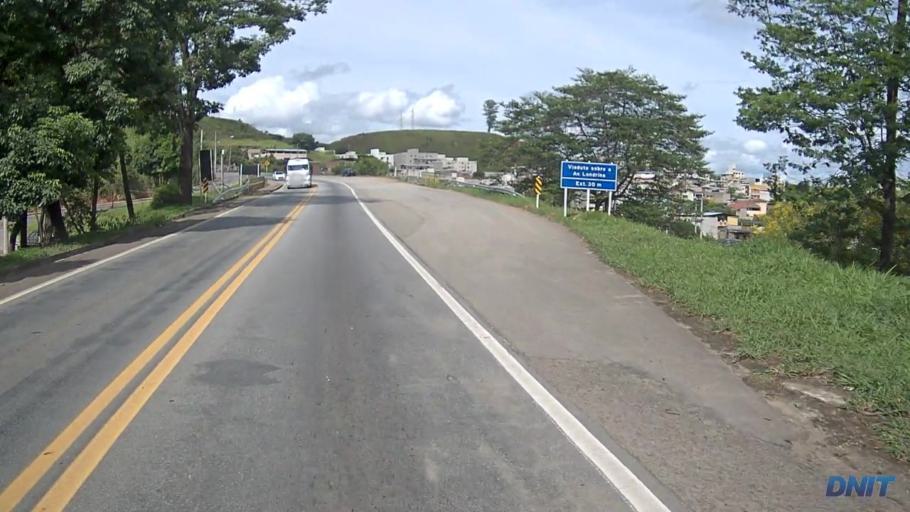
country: BR
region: Minas Gerais
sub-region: Ipatinga
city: Ipatinga
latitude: -19.4614
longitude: -42.5284
